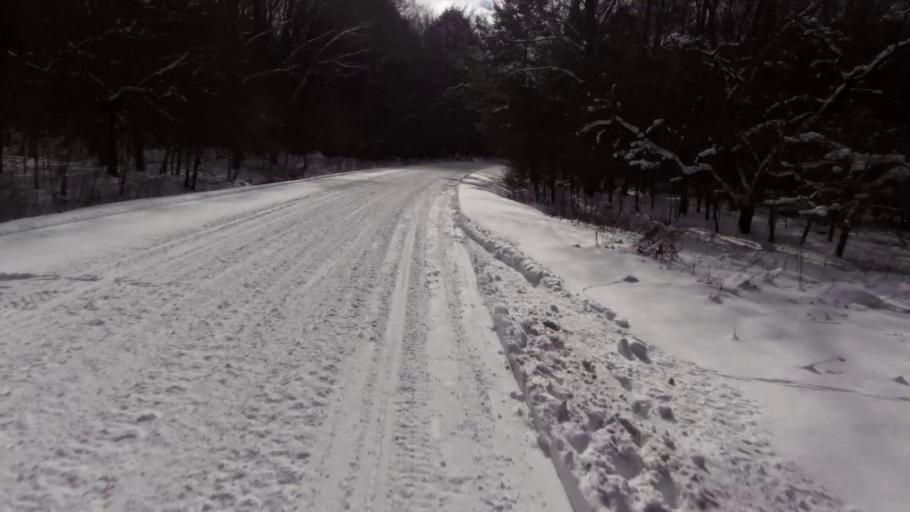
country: US
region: New York
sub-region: Cattaraugus County
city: Salamanca
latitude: 42.0849
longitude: -78.7480
